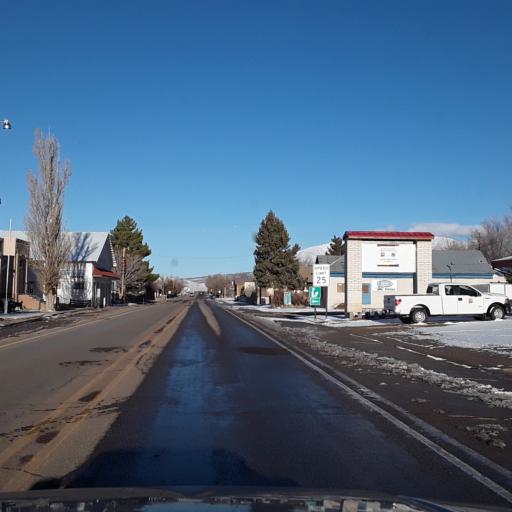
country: US
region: New Mexico
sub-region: Lincoln County
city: Carrizozo
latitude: 33.6427
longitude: -105.8767
